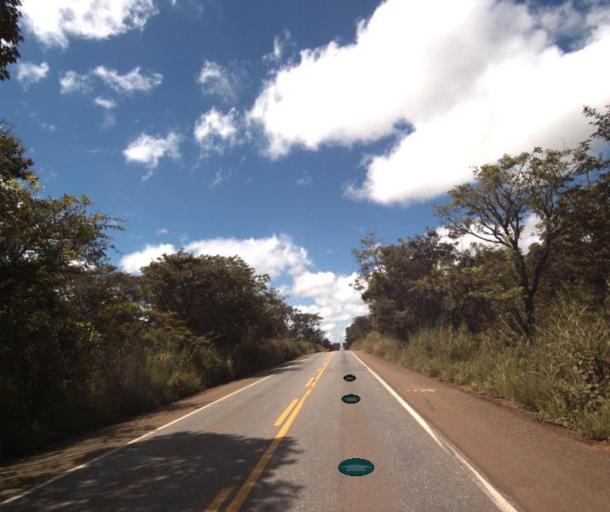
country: BR
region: Goias
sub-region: Jaragua
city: Jaragua
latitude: -15.9078
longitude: -49.2268
